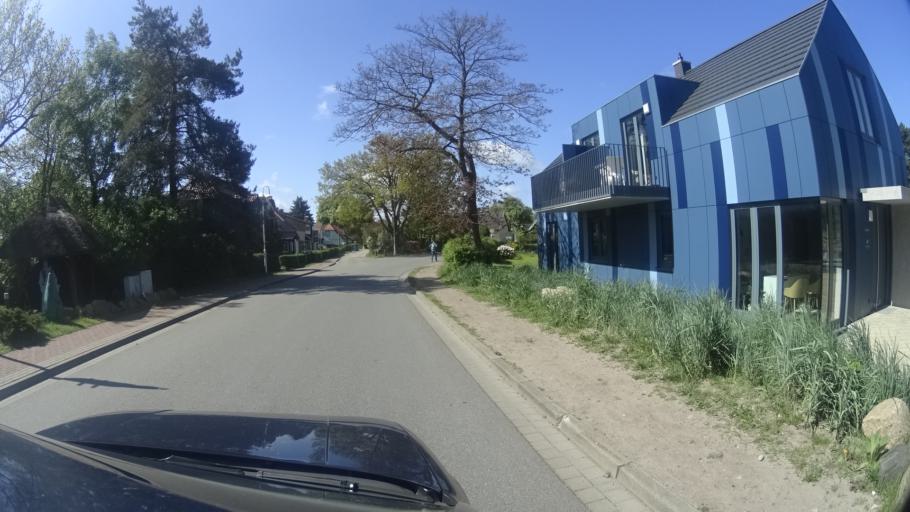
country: DE
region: Mecklenburg-Vorpommern
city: Ostseebad Prerow
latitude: 54.4446
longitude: 12.5819
